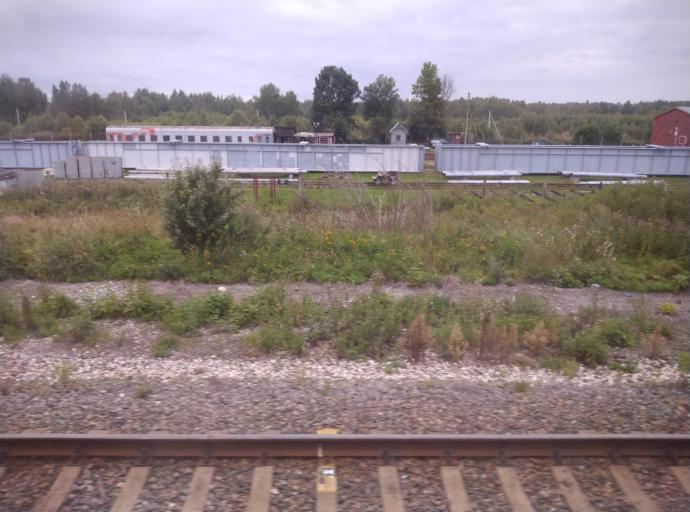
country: RU
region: Kostroma
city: Kosmynino
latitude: 57.5905
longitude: 40.7654
